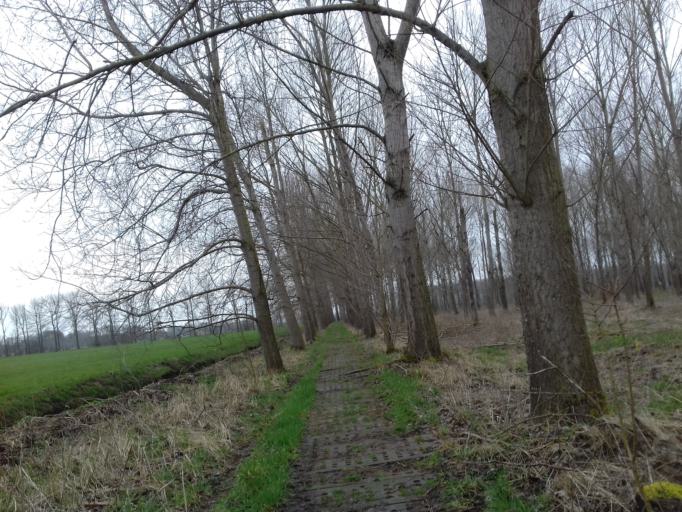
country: NL
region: Gelderland
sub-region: Gemeente Culemborg
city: Culemborg
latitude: 51.9059
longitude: 5.2220
